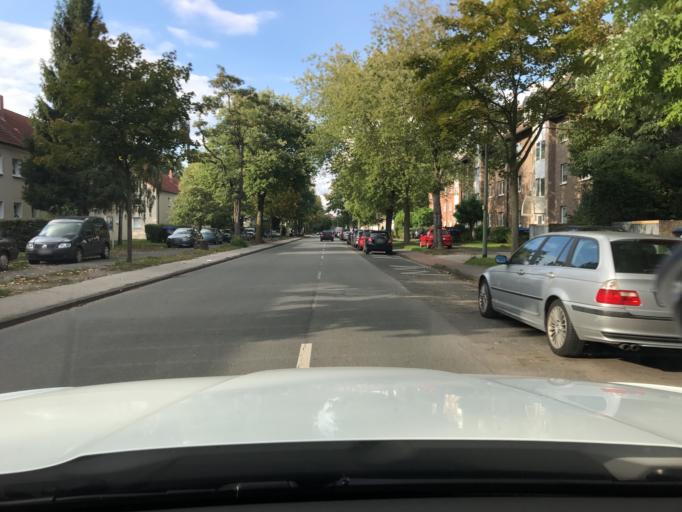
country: DE
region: North Rhine-Westphalia
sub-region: Regierungsbezirk Dusseldorf
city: Hochfeld
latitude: 51.3708
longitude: 6.7432
